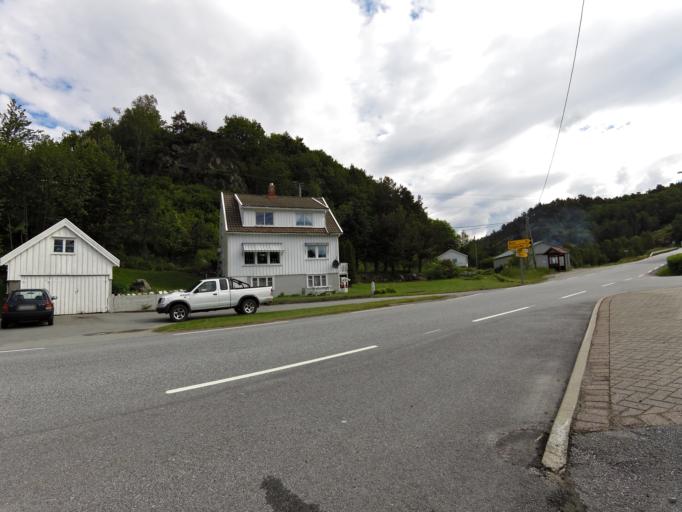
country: NO
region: Vest-Agder
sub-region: Lindesnes
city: Vigeland
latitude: 58.0505
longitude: 7.2003
